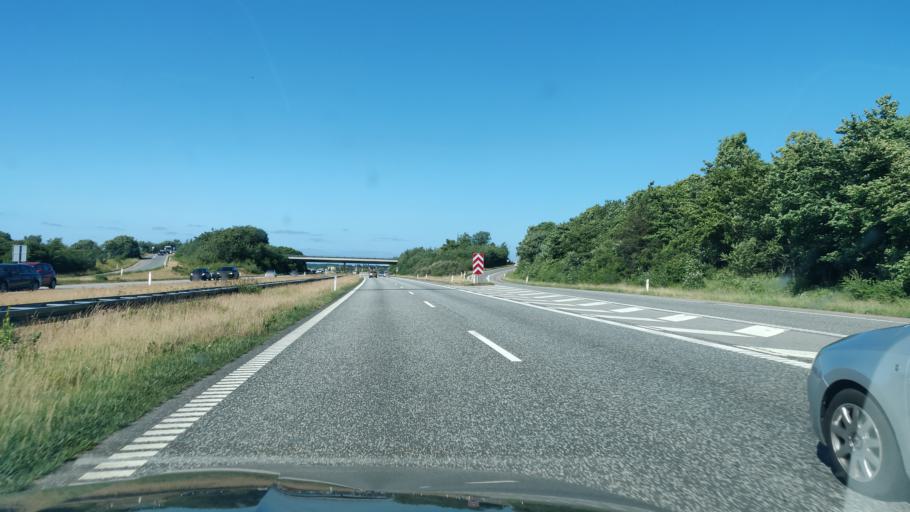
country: DK
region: North Denmark
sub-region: Rebild Kommune
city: Stovring
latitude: 56.8773
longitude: 9.8008
